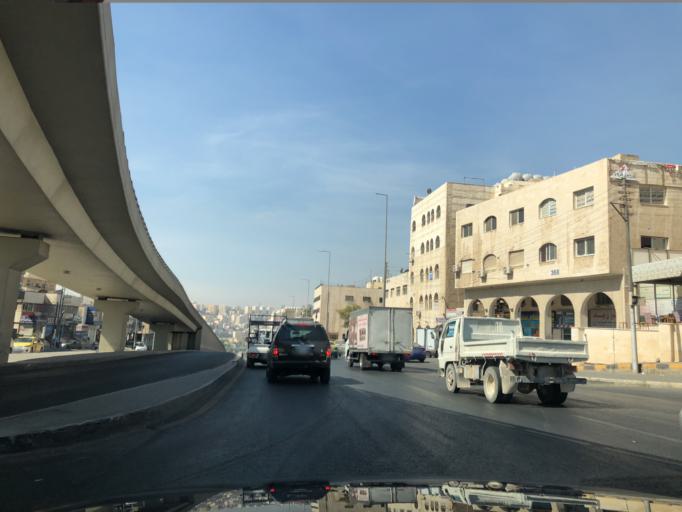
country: JO
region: Amman
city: Al Jubayhah
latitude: 32.0247
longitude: 35.8543
